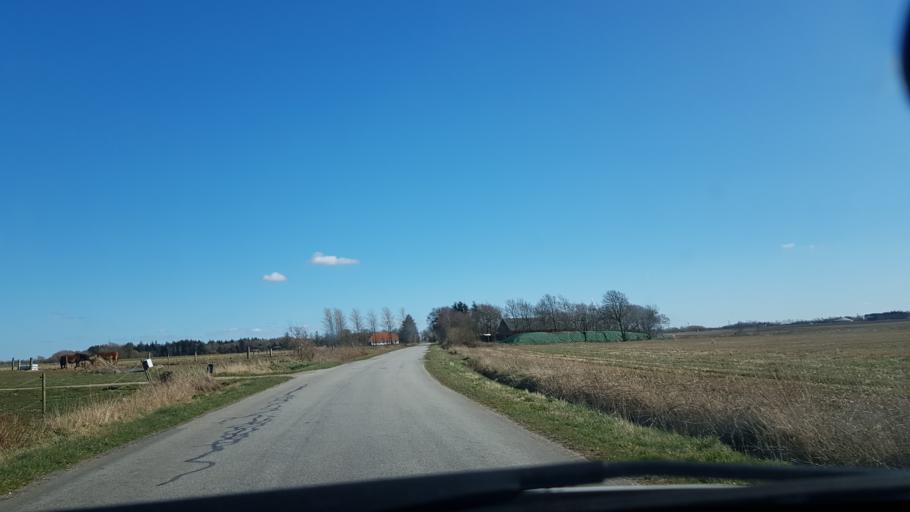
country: DK
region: South Denmark
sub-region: Tonder Kommune
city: Sherrebek
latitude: 55.2278
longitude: 8.7972
